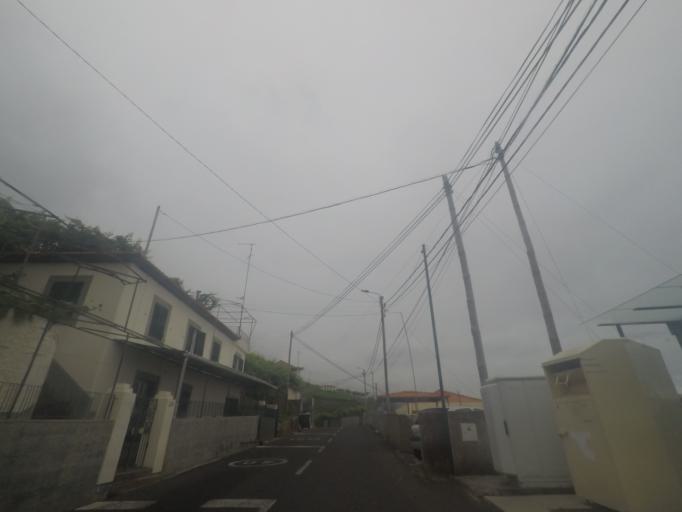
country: PT
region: Madeira
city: Camara de Lobos
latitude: 32.6714
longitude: -16.9700
